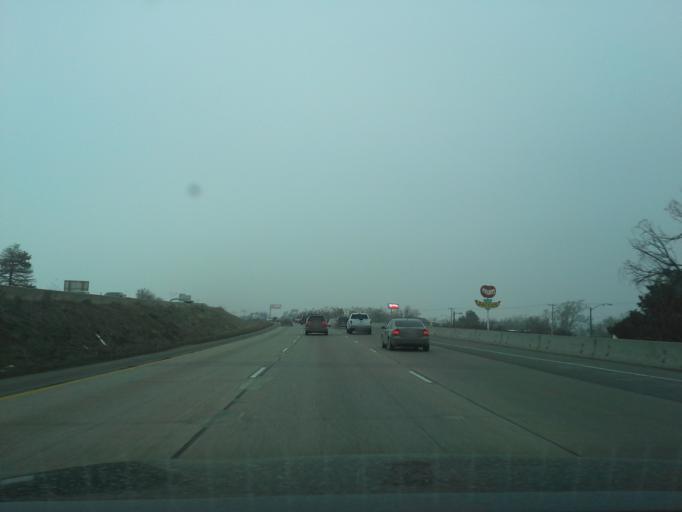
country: US
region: Utah
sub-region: Weber County
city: Roy
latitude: 41.1541
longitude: -112.0252
